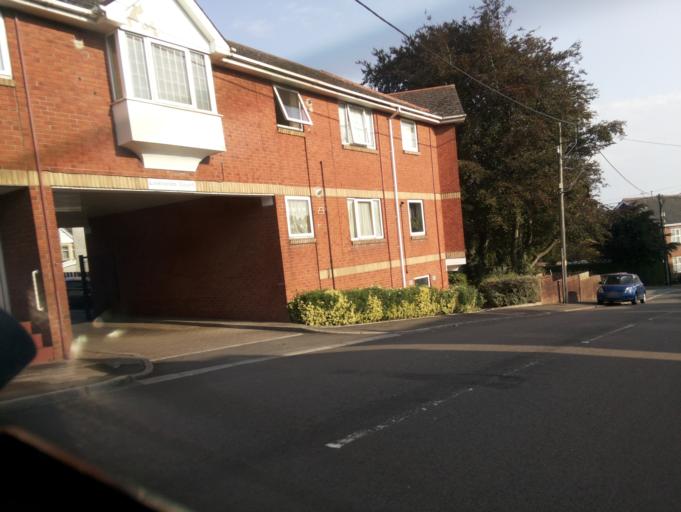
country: GB
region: Wales
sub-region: Torfaen County Borough
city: Cwmbran
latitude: 51.6645
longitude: -3.0257
